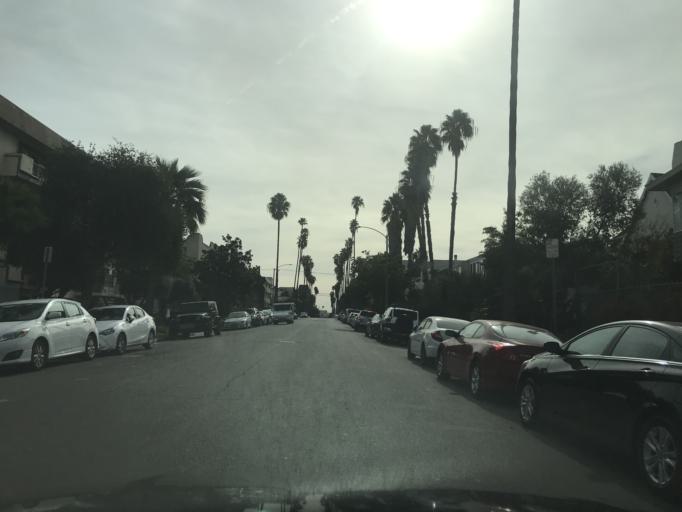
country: US
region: California
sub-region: Los Angeles County
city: Hollywood
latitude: 34.0668
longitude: -118.3128
